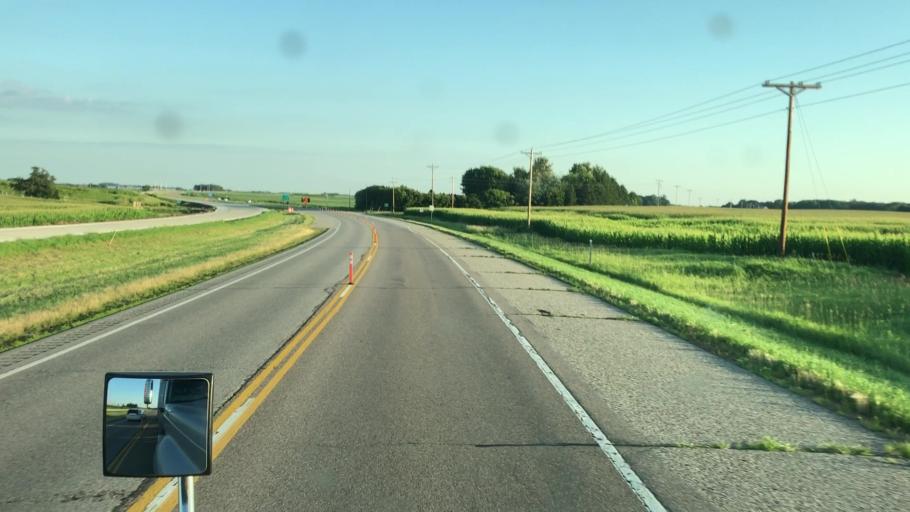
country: US
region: Minnesota
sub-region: Scott County
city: Belle Plaine
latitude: 44.5599
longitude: -93.8510
